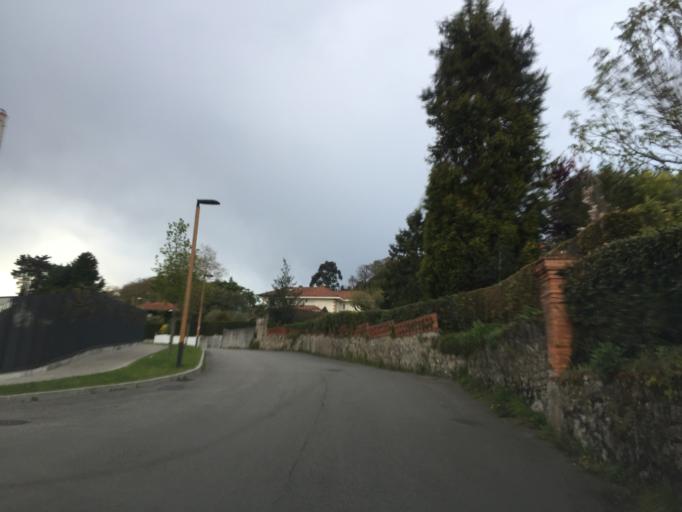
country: ES
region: Asturias
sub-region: Province of Asturias
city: Gijon
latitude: 43.5392
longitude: -5.6223
